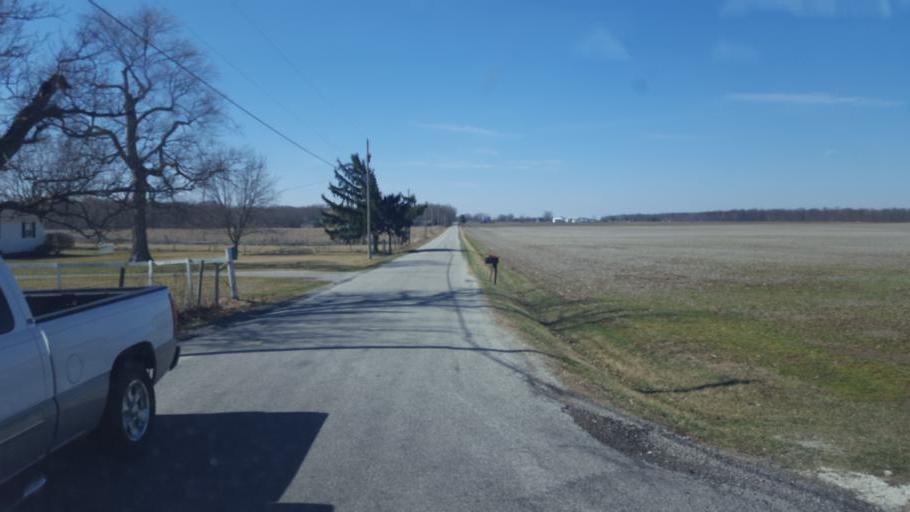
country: US
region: Ohio
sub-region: Marion County
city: Marion
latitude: 40.4986
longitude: -83.0919
